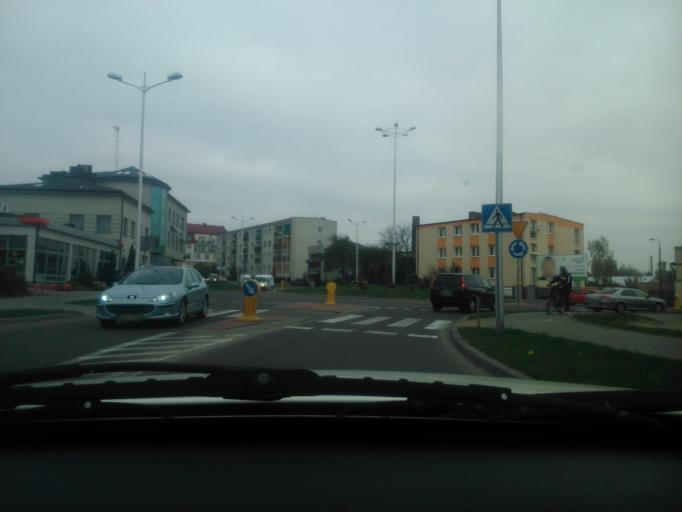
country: PL
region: Masovian Voivodeship
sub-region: Powiat mlawski
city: Mlawa
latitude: 53.1091
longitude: 20.3830
